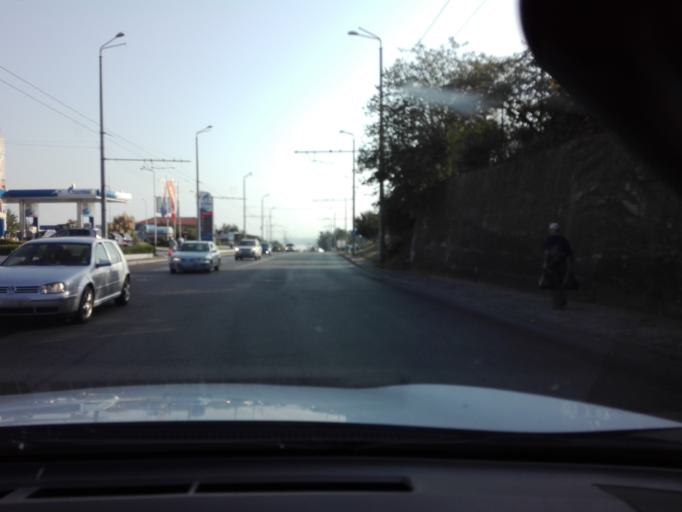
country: BG
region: Burgas
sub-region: Obshtina Burgas
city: Burgas
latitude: 42.4610
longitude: 27.4089
